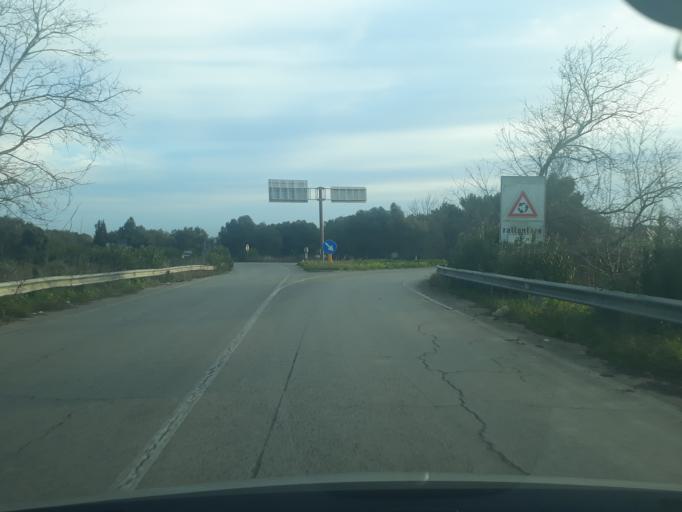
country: IT
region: Apulia
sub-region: Provincia di Brindisi
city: Brindisi
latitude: 40.6546
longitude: 17.9034
